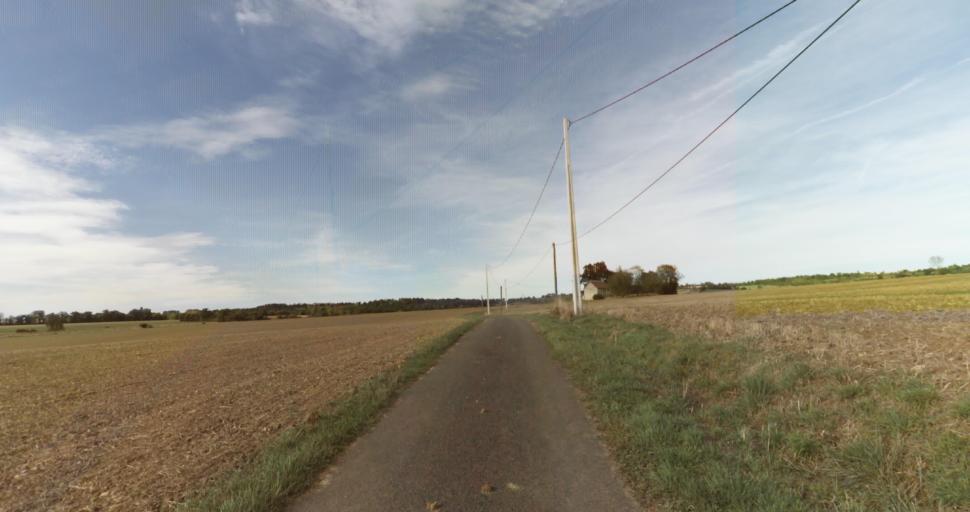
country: FR
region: Lower Normandy
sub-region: Departement de l'Orne
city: Gace
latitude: 48.7134
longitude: 0.2576
